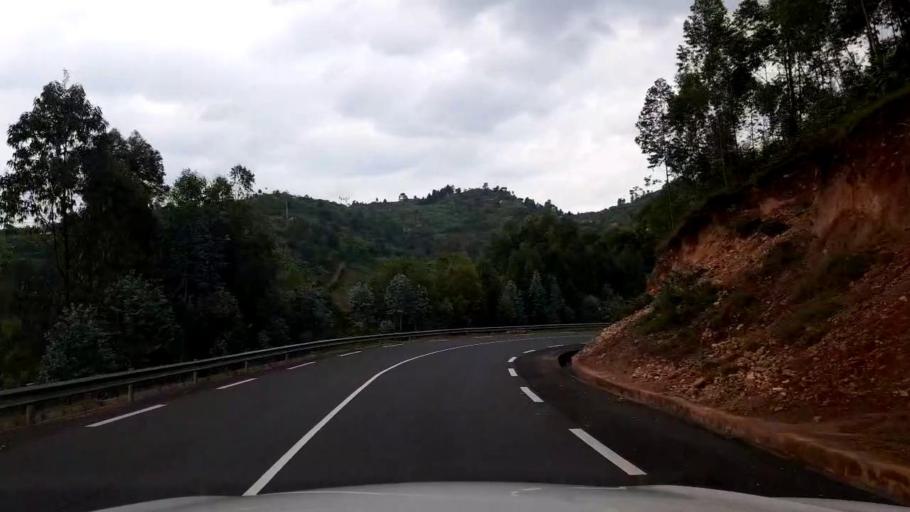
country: RW
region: Western Province
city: Kibuye
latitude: -1.9074
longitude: 29.3658
